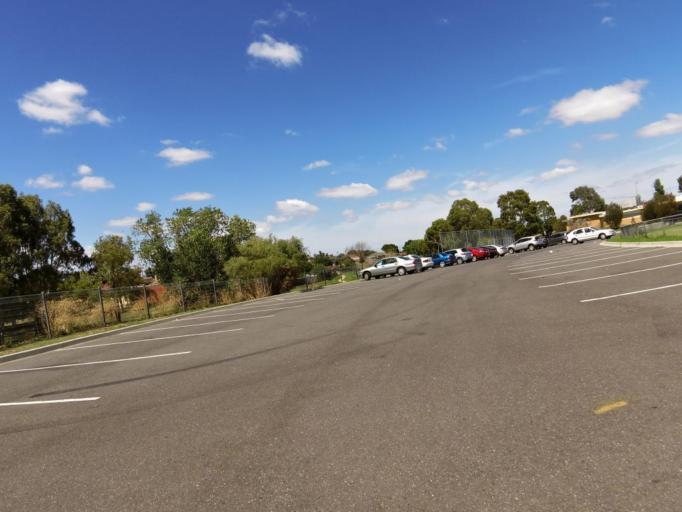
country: AU
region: Victoria
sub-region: Whittlesea
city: Thomastown
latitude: -37.6779
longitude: 145.0076
